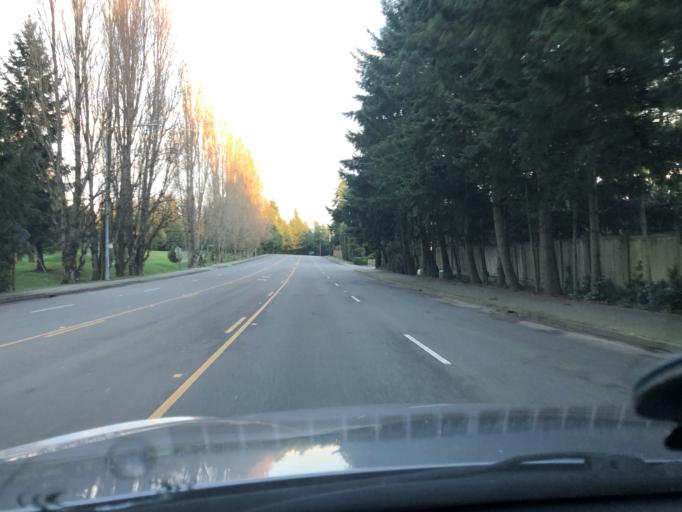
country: US
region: Washington
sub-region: Pierce County
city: Fife Heights
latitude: 47.3152
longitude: -122.3861
